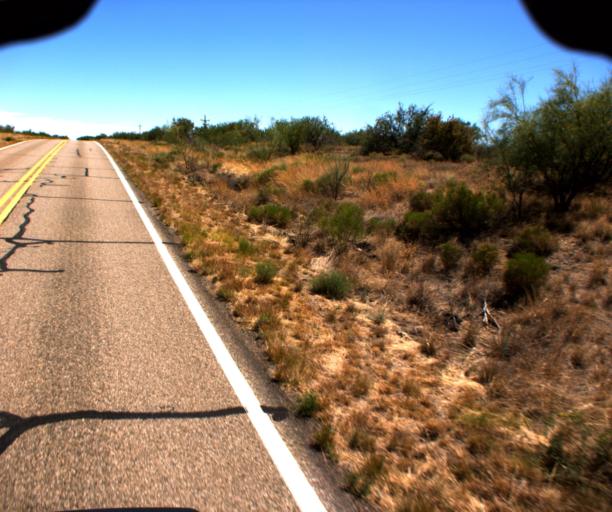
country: US
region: Arizona
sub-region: Pima County
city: Three Points
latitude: 31.7134
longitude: -111.4878
